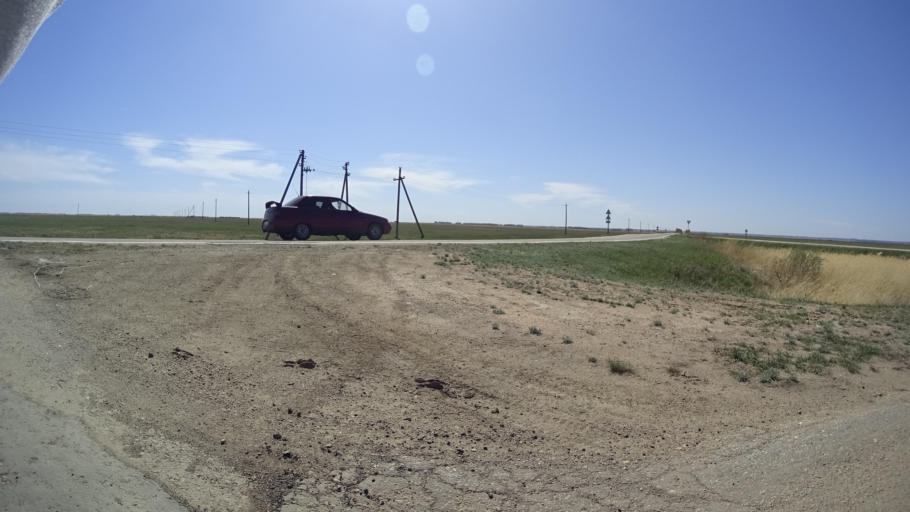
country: RU
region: Chelyabinsk
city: Chesma
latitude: 53.8039
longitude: 61.0118
